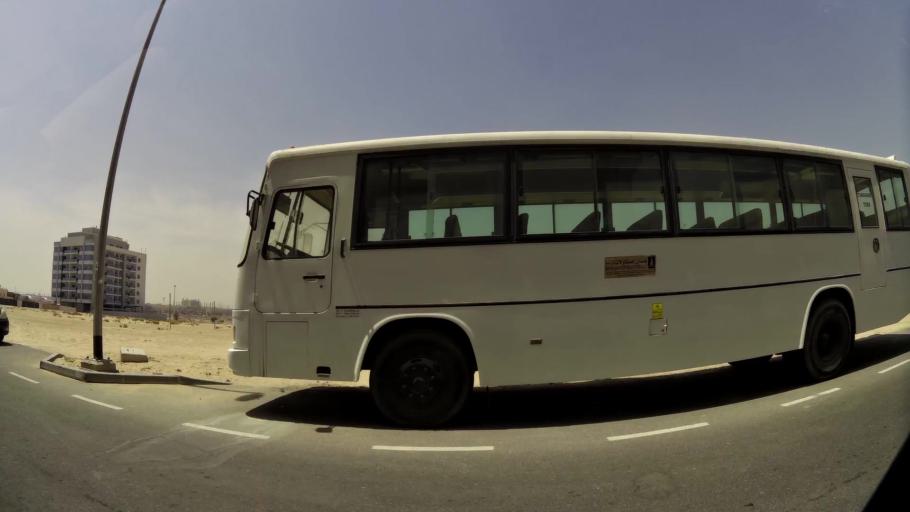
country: AE
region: Ash Shariqah
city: Sharjah
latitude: 25.1815
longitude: 55.4065
